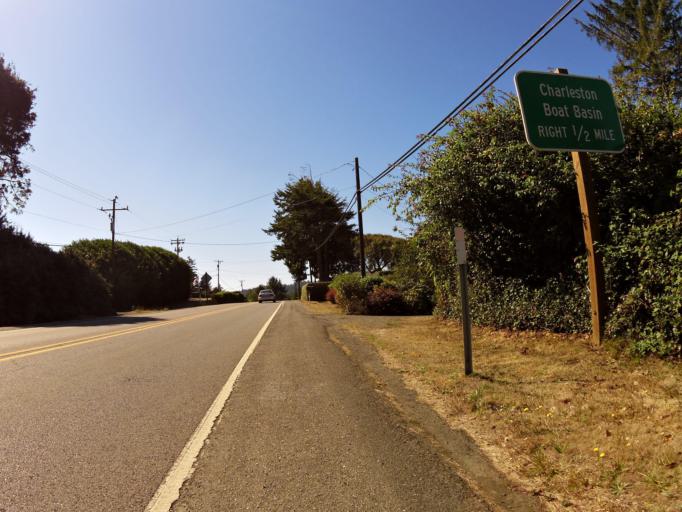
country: US
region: Oregon
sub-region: Coos County
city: Barview
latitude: 43.3422
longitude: -124.3153
